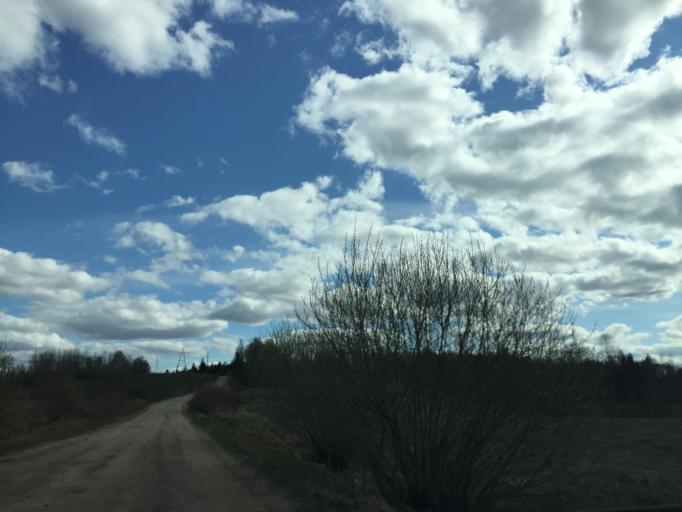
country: LV
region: Rezekne
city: Rezekne
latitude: 56.6448
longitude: 27.2910
